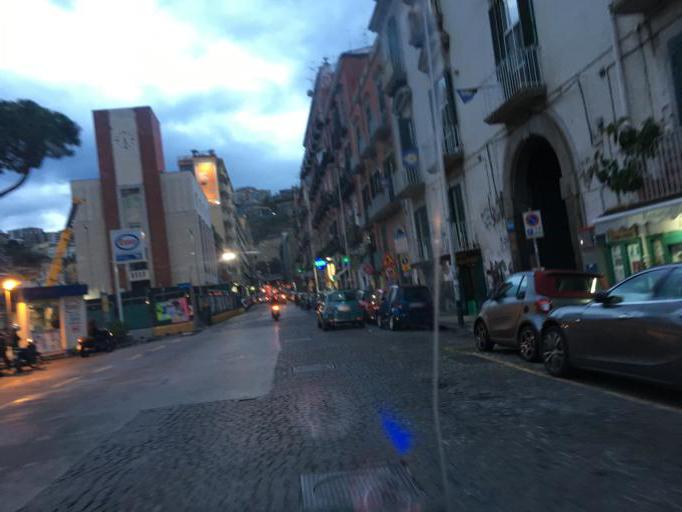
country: IT
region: Campania
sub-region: Provincia di Napoli
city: Napoli
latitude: 40.8320
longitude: 14.2242
